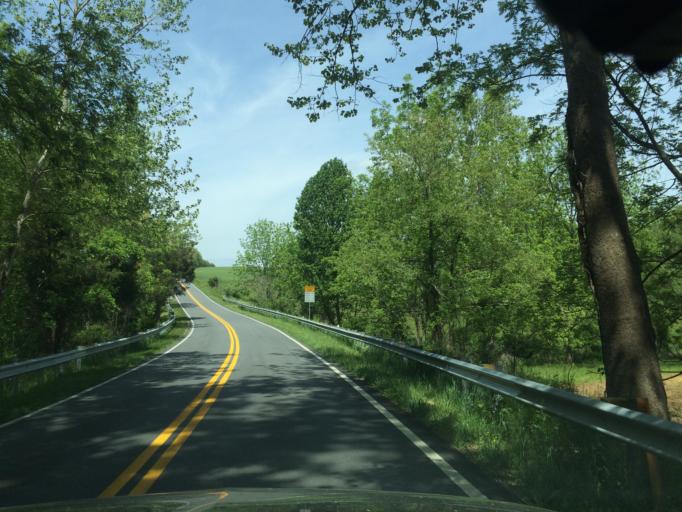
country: US
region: Maryland
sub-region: Carroll County
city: Westminster
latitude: 39.5183
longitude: -76.9502
